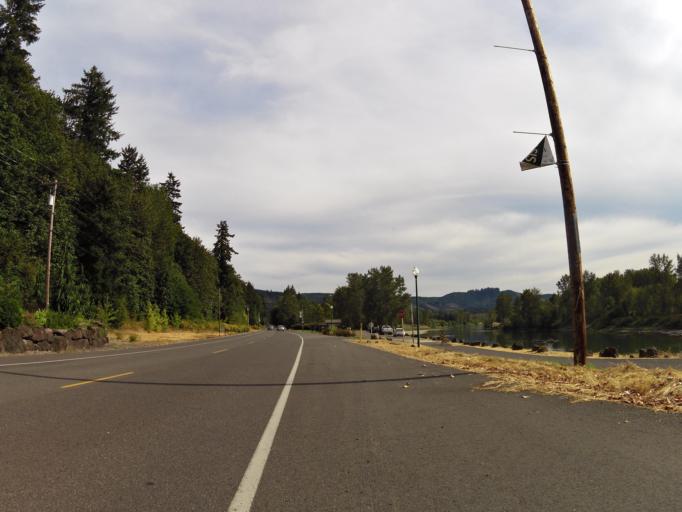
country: US
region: Washington
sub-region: Cowlitz County
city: Castle Rock
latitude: 46.2665
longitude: -122.9034
